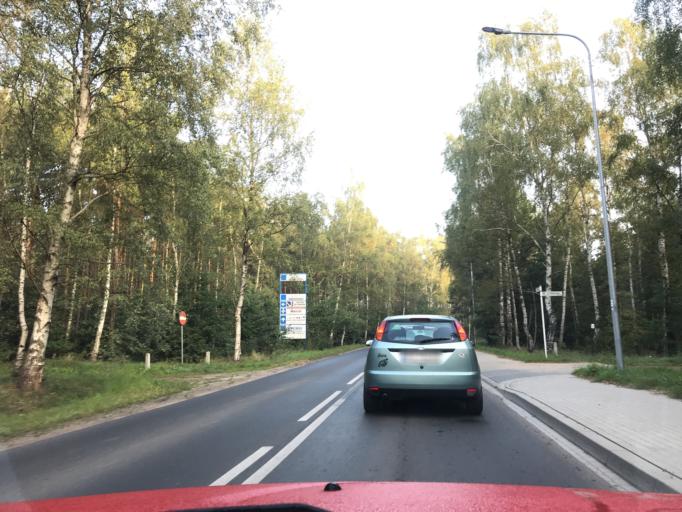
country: PL
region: Greater Poland Voivodeship
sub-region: Powiat poznanski
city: Baranowo
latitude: 52.4115
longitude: 16.7910
